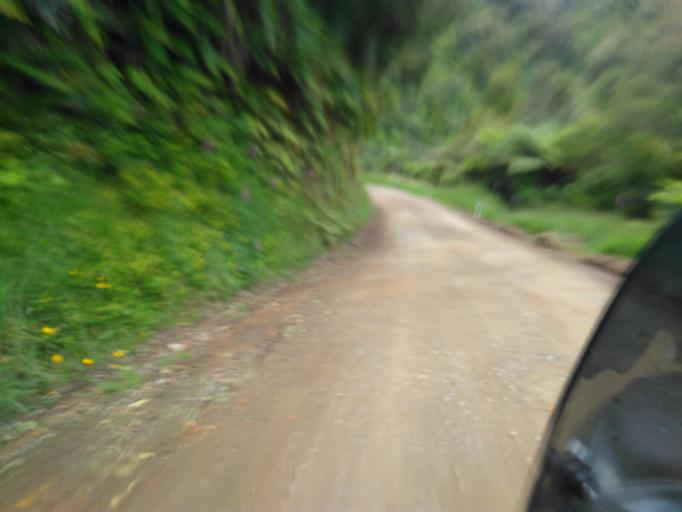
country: NZ
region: Bay of Plenty
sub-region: Opotiki District
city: Opotiki
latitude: -38.0905
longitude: 177.4813
